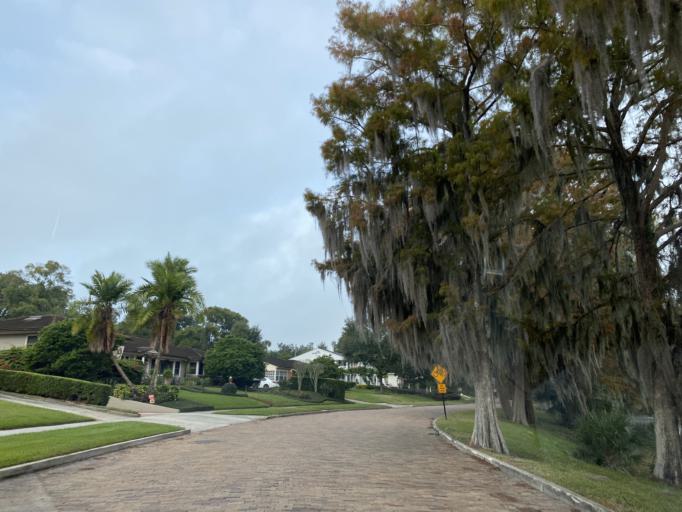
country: US
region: Florida
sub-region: Orange County
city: Orlando
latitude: 28.5580
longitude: -81.3891
